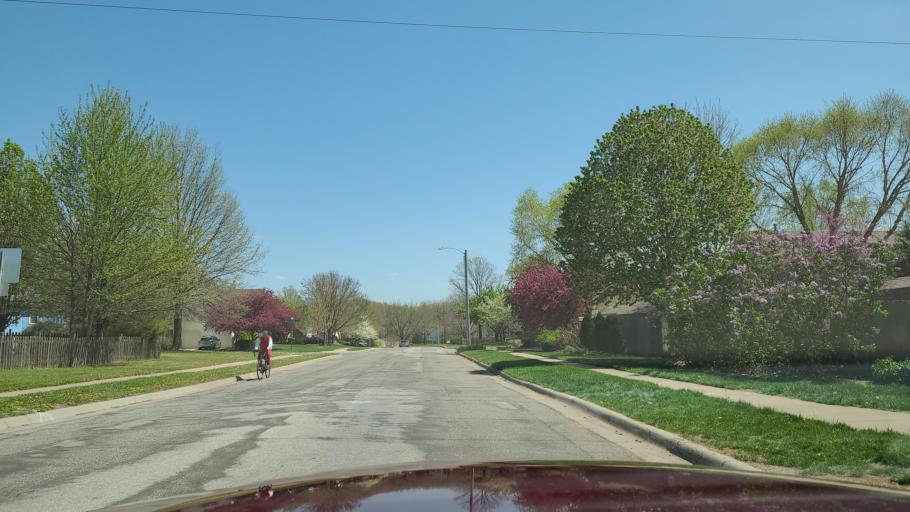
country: US
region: Kansas
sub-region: Douglas County
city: Lawrence
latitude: 38.9658
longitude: -95.2957
